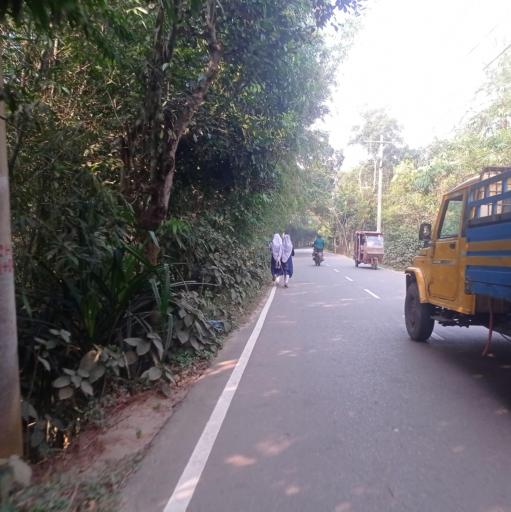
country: BD
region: Dhaka
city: Bhairab Bazar
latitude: 24.0676
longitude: 90.8416
